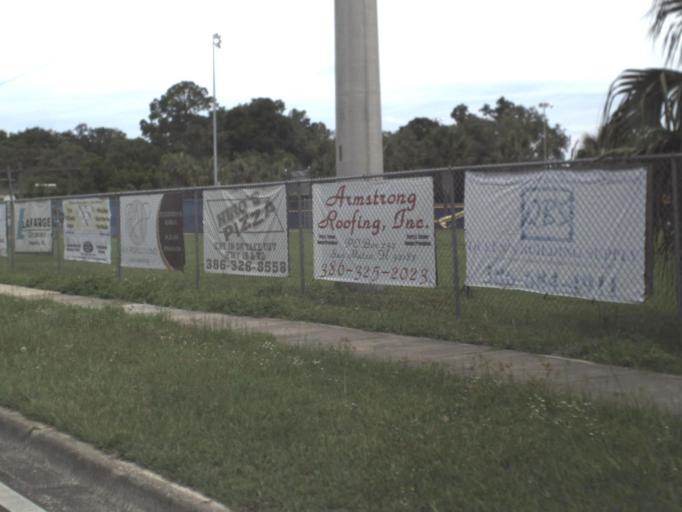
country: US
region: Florida
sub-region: Putnam County
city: Palatka
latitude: 29.6416
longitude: -81.6681
